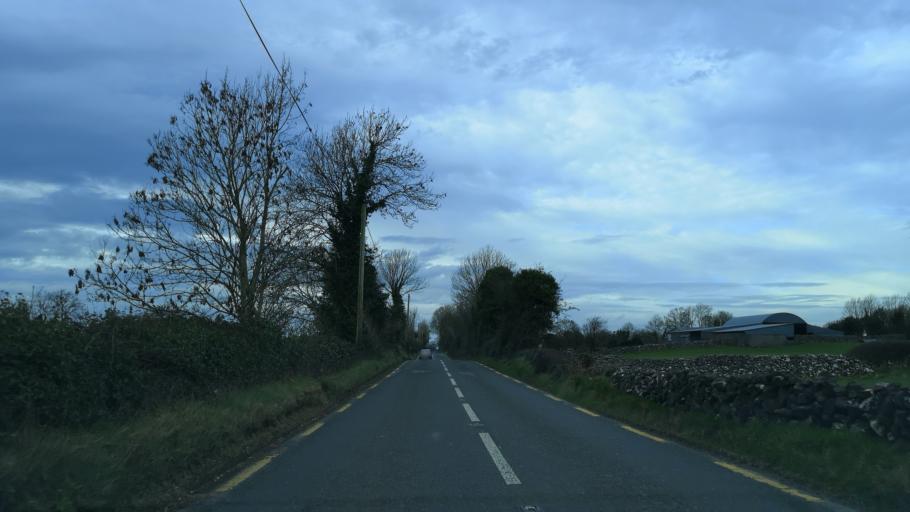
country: IE
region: Connaught
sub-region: County Galway
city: Loughrea
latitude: 53.2034
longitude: -8.4704
